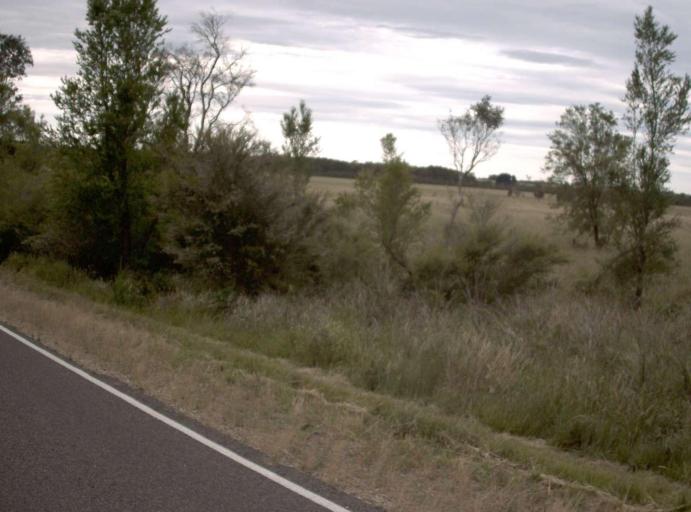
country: AU
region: Victoria
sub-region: East Gippsland
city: Bairnsdale
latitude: -37.9886
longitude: 147.3980
